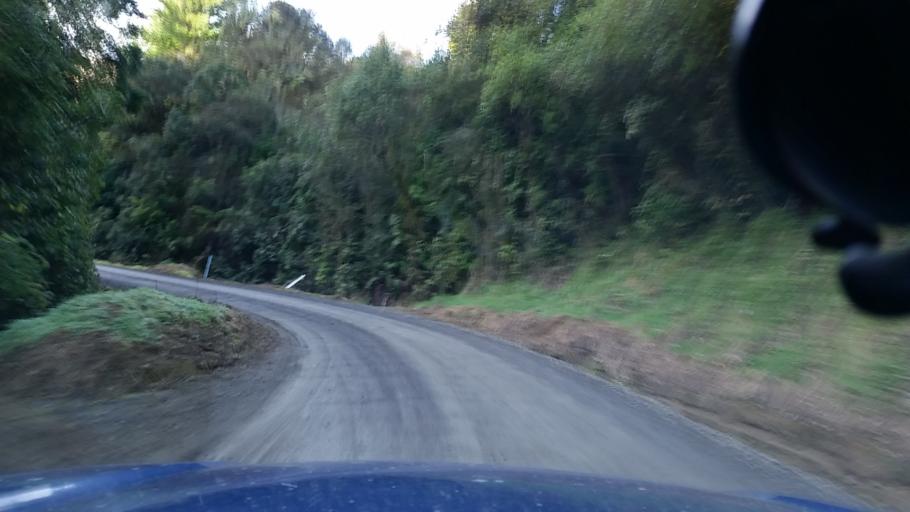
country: NZ
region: Taranaki
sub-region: New Plymouth District
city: Waitara
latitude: -39.0613
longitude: 174.7860
